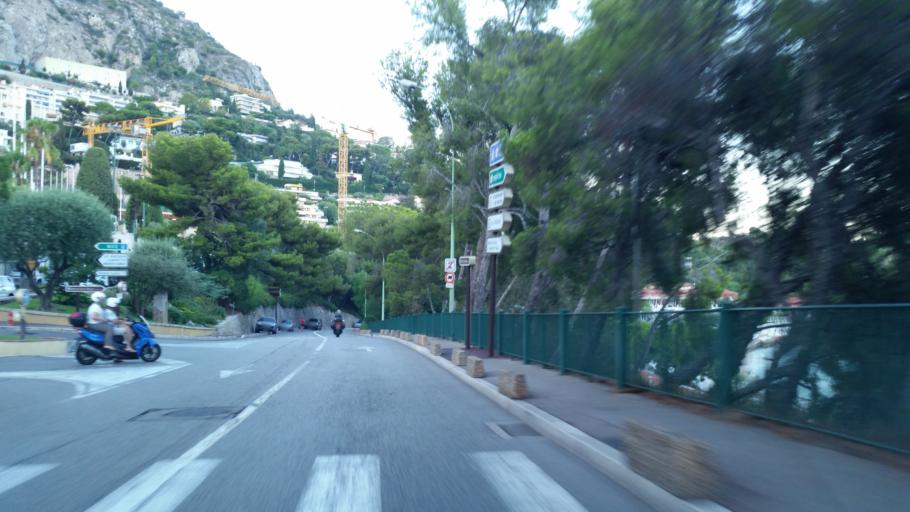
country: MC
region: Commune de Monaco
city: Saint-Roman
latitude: 43.7505
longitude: 7.4400
